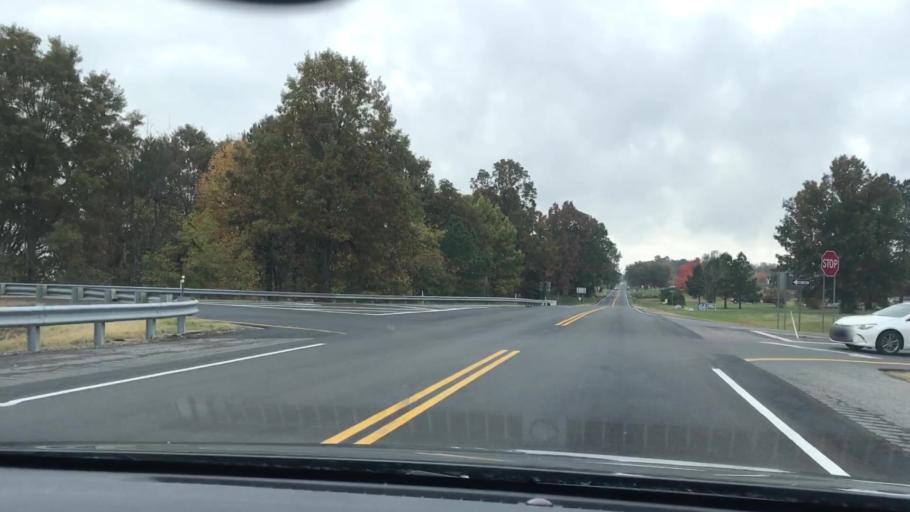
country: US
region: Kentucky
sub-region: Graves County
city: Mayfield
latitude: 36.7749
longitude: -88.5959
